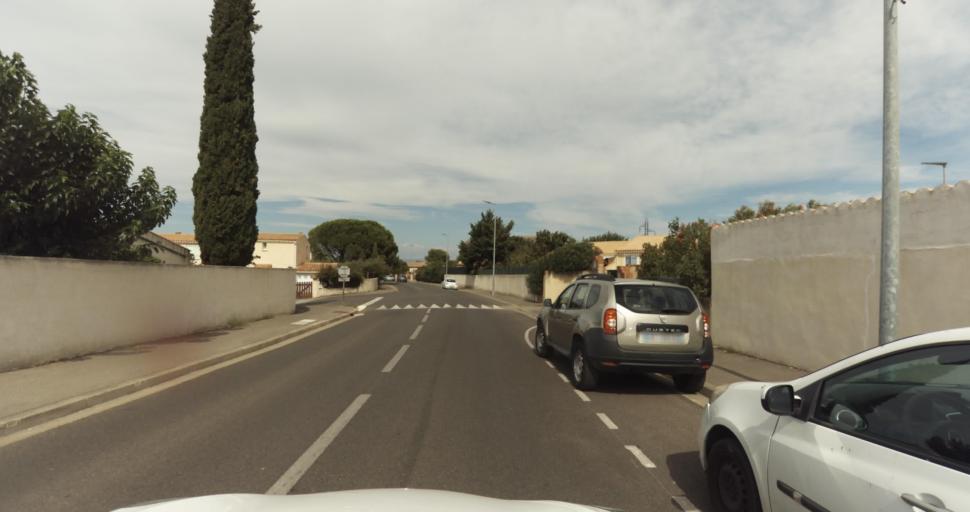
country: FR
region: Provence-Alpes-Cote d'Azur
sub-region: Departement des Bouches-du-Rhone
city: Miramas
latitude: 43.5738
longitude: 5.0064
